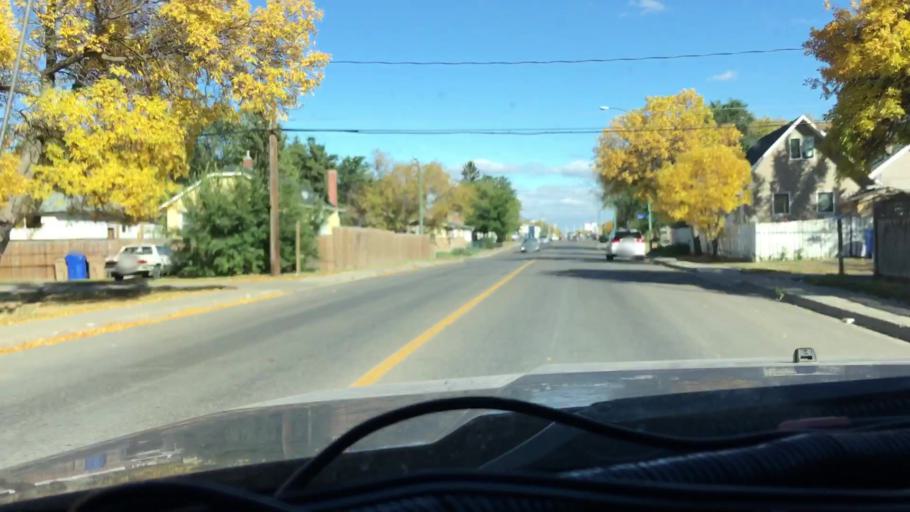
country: CA
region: Saskatchewan
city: Regina
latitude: 50.4629
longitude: -104.6221
